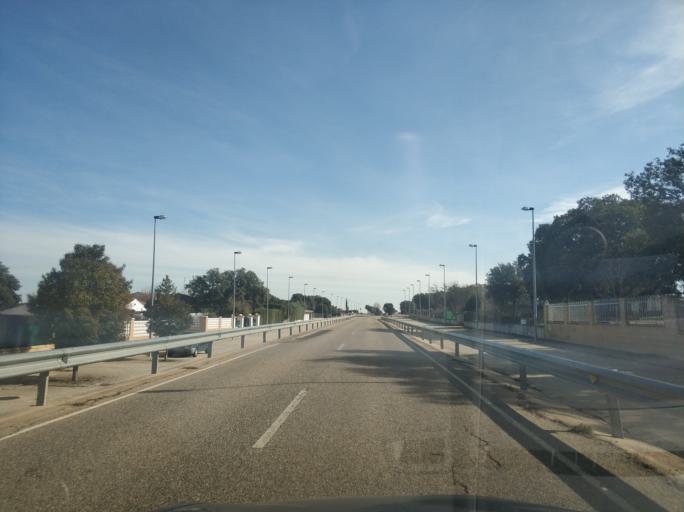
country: ES
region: Castille and Leon
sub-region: Provincia de Salamanca
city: Florida de Liebana
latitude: 41.0187
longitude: -5.7453
